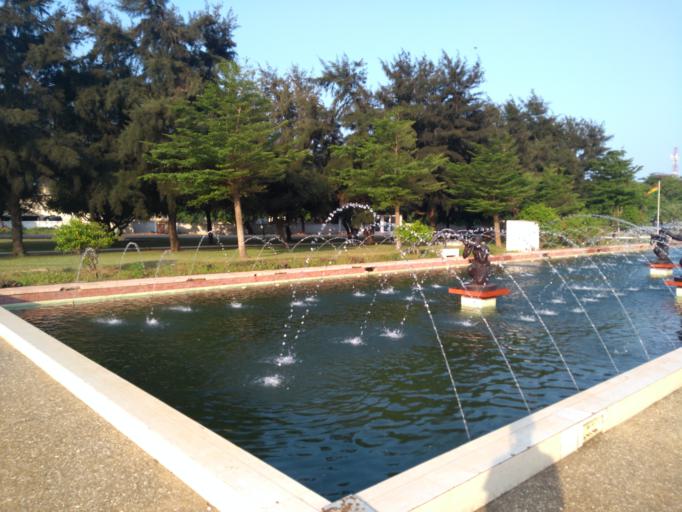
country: GH
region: Greater Accra
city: Accra
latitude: 5.5450
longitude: -0.2032
